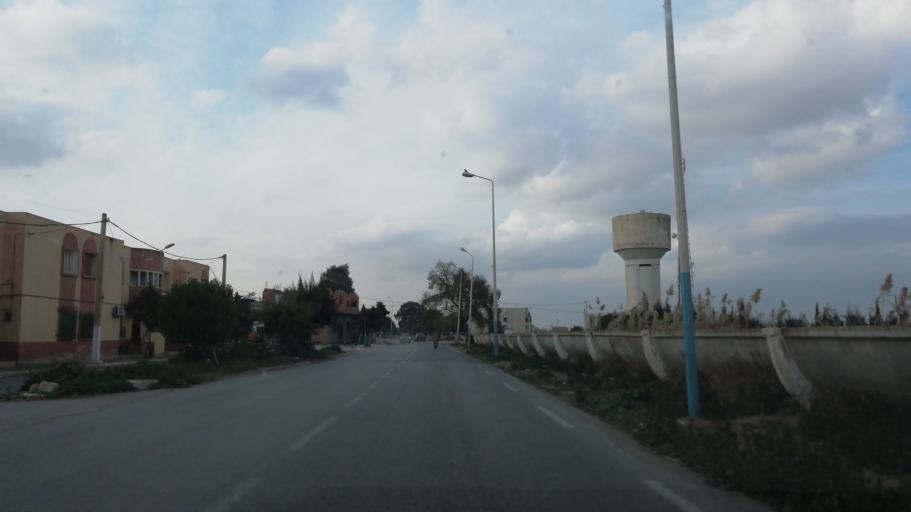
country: DZ
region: Mascara
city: Sig
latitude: 35.6550
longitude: 0.0167
